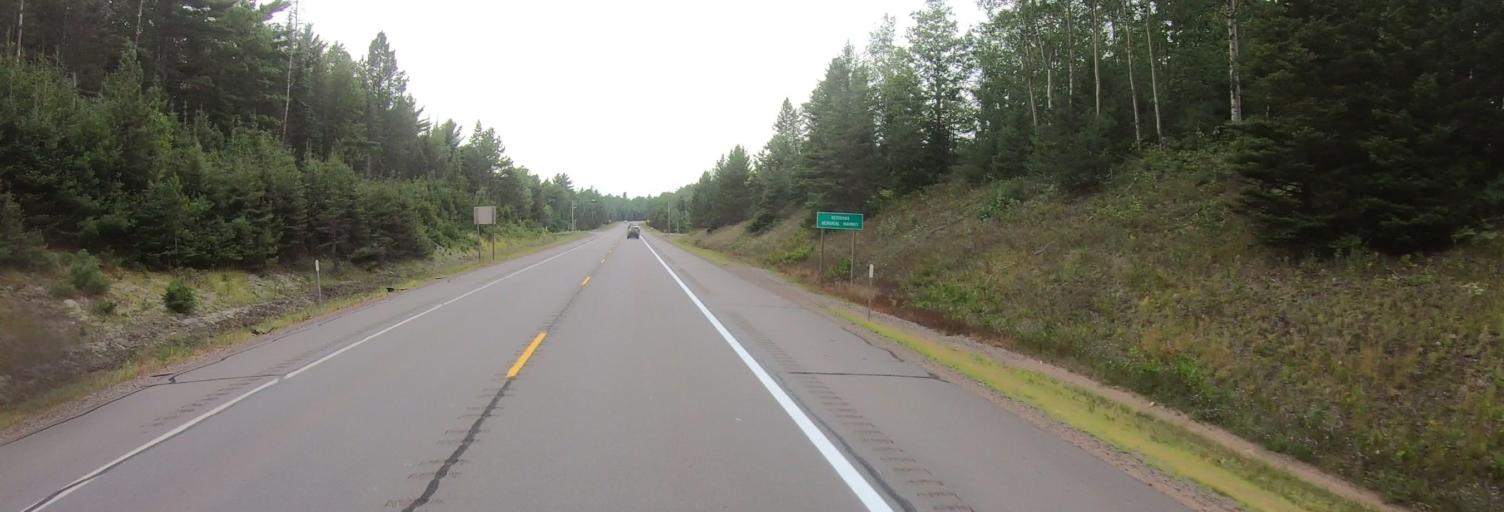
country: US
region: Michigan
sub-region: Marquette County
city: West Ishpeming
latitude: 46.4968
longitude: -87.9267
